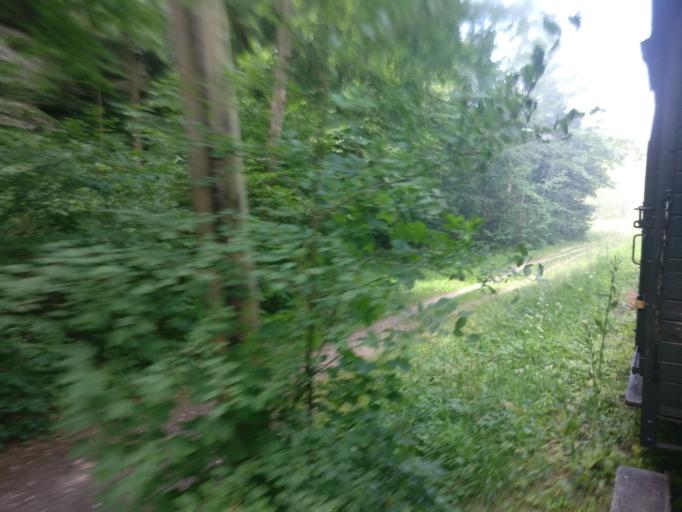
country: AT
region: Upper Austria
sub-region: Politischer Bezirk Steyr-Land
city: Garsten
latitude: 48.0443
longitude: 14.3700
